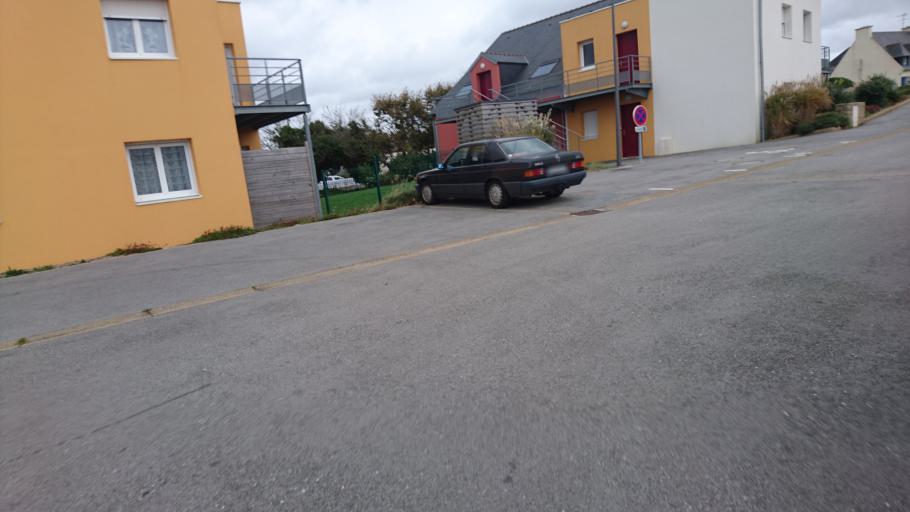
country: FR
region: Brittany
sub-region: Departement du Finistere
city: Lampaul-Plouarzel
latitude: 48.4490
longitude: -4.7614
